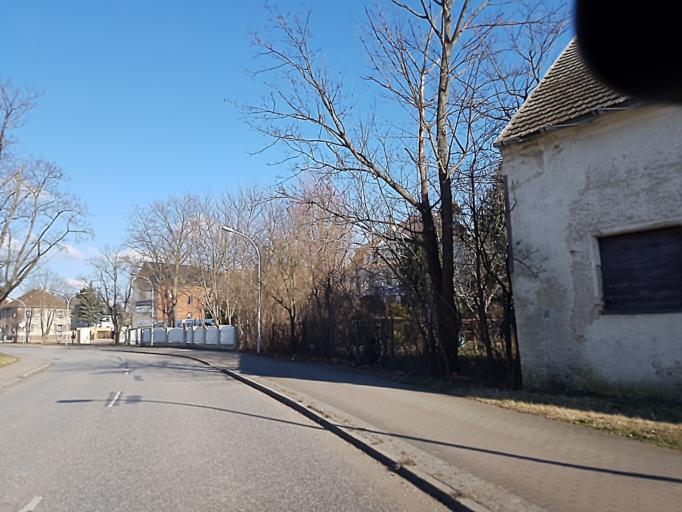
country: DE
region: Brandenburg
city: Doberlug-Kirchhain
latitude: 51.6366
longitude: 13.5655
